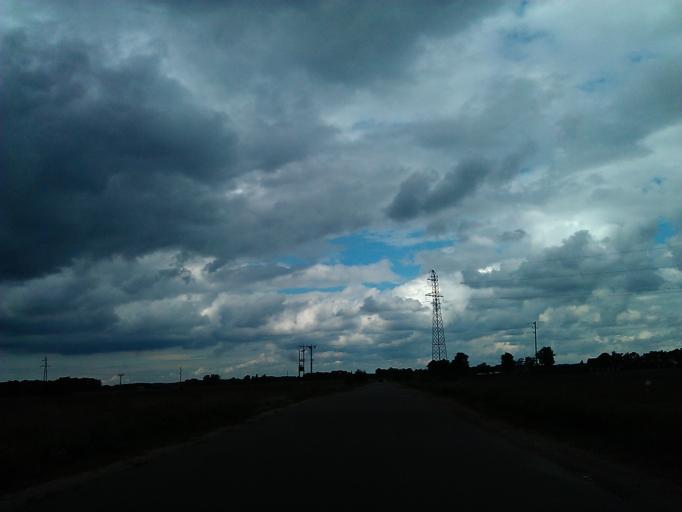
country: LV
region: Adazi
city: Adazi
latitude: 57.0891
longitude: 24.3011
